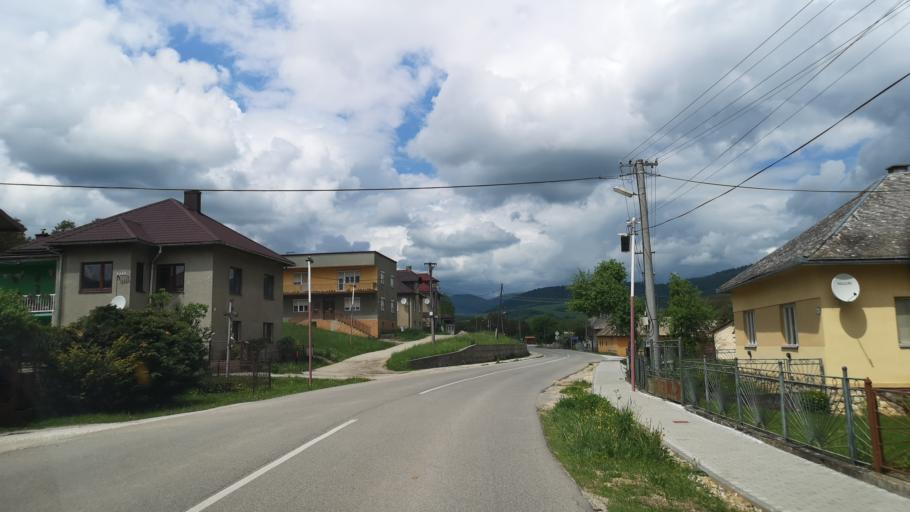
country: SK
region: Kosicky
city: Dobsina
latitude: 48.6892
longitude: 20.3472
